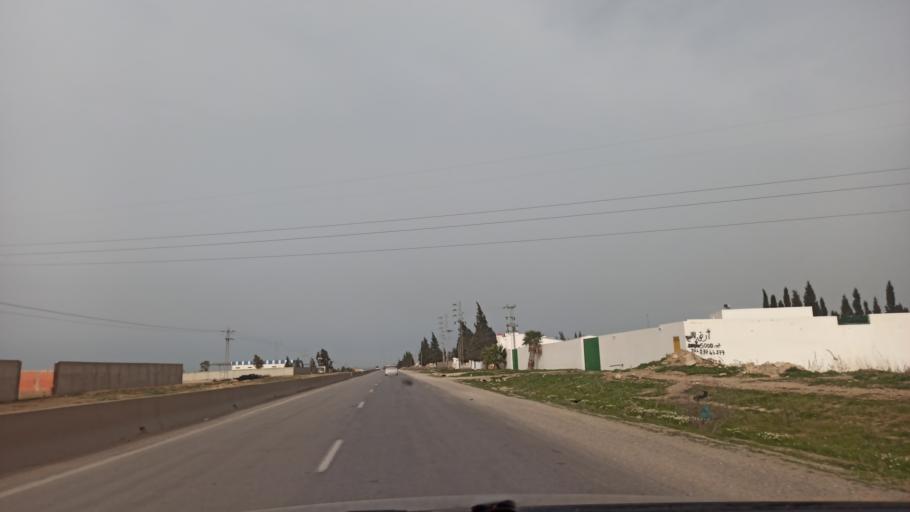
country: TN
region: Tunis
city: La Mohammedia
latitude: 36.5716
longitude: 10.0872
